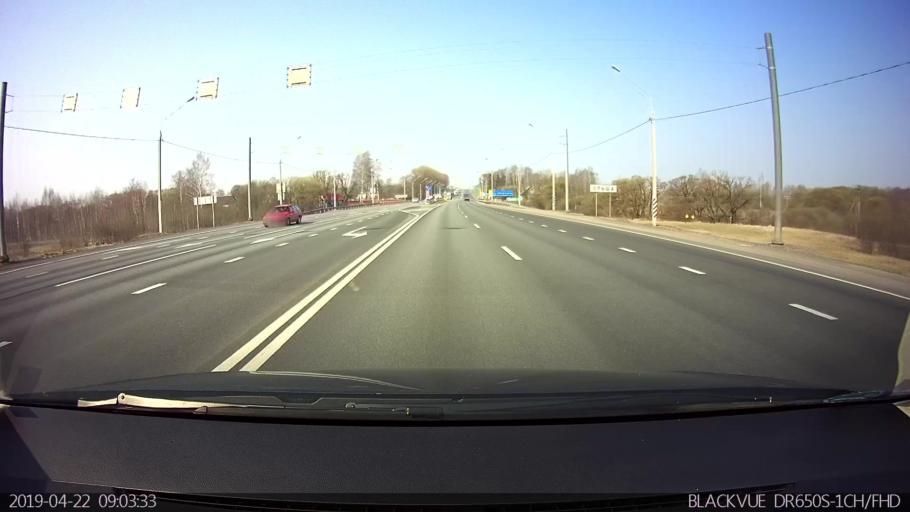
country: RU
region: Smolensk
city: Pechersk
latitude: 54.8514
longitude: 31.8567
